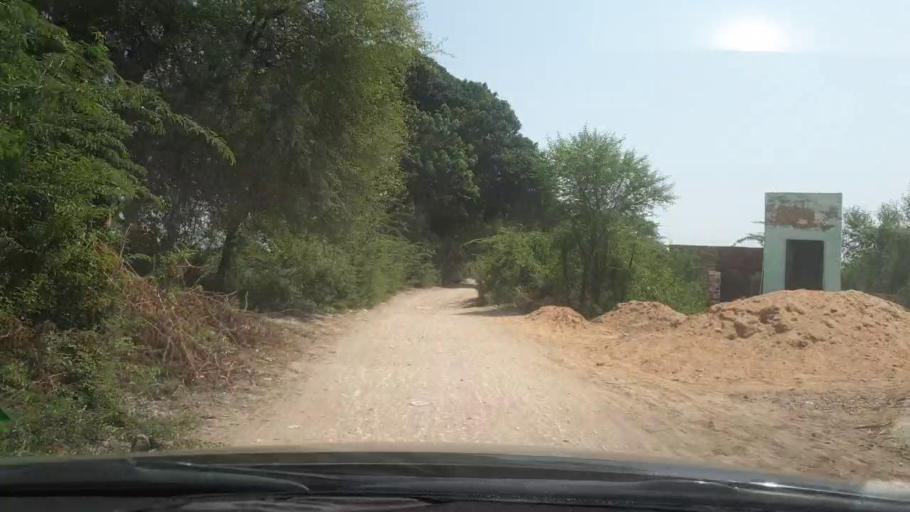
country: PK
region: Sindh
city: Naukot
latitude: 24.7694
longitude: 69.1943
